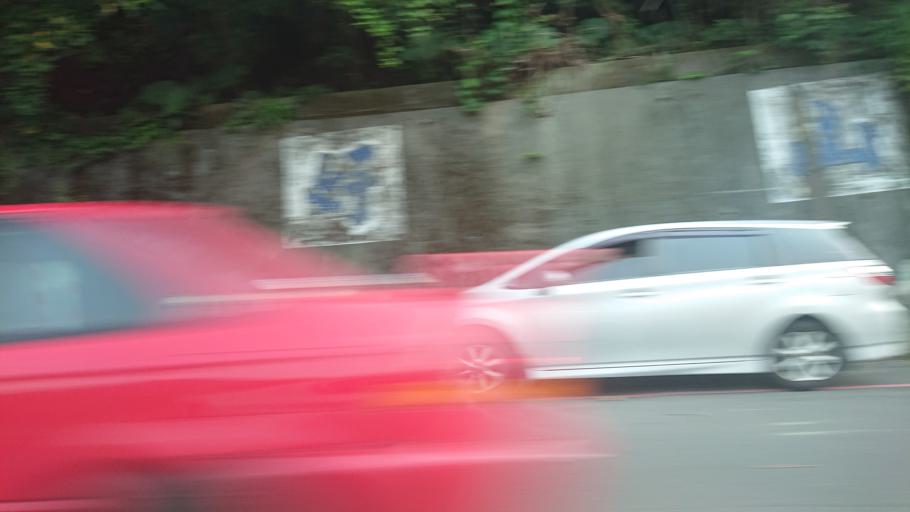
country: TW
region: Taiwan
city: Daxi
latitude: 24.8707
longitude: 121.4110
